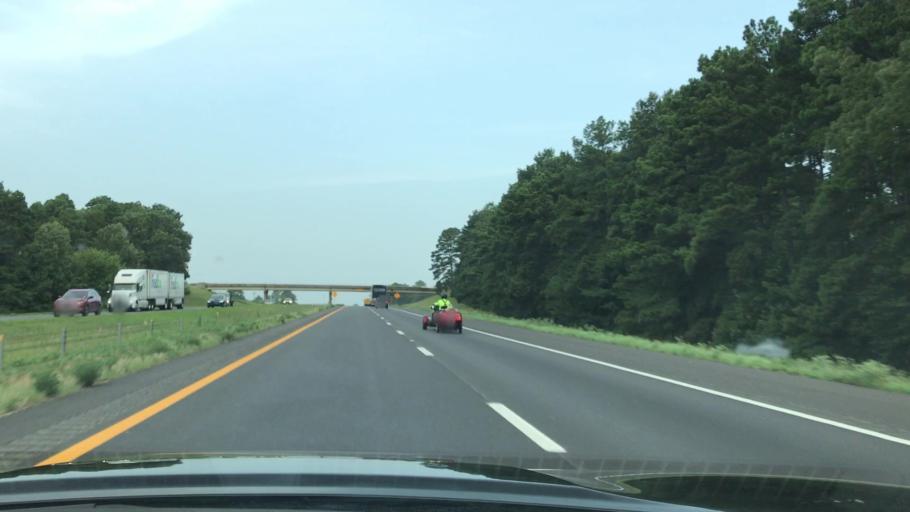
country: US
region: Texas
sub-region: Harrison County
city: Hallsville
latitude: 32.4673
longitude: -94.6183
